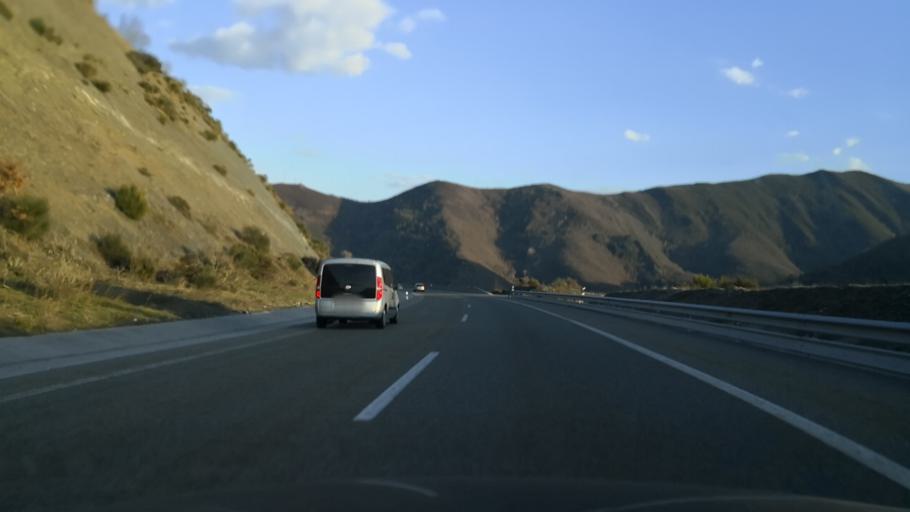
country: ES
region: Castille and Leon
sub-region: Provincia de Leon
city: Vega de Valcarce
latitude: 42.6772
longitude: -6.9883
